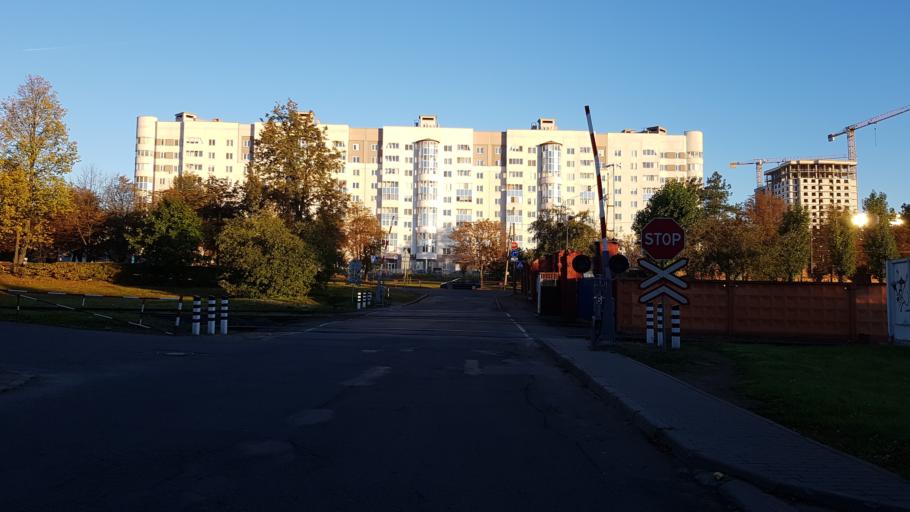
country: BY
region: Minsk
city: Syenitsa
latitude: 53.8792
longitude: 27.5206
